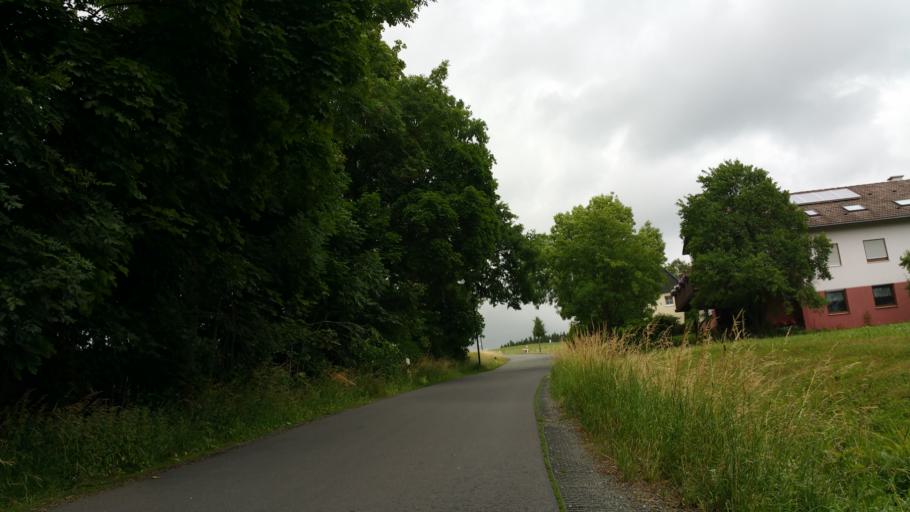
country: DE
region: Bavaria
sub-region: Upper Franconia
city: Schwarzenbach an der Saale
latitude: 50.2260
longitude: 11.9697
